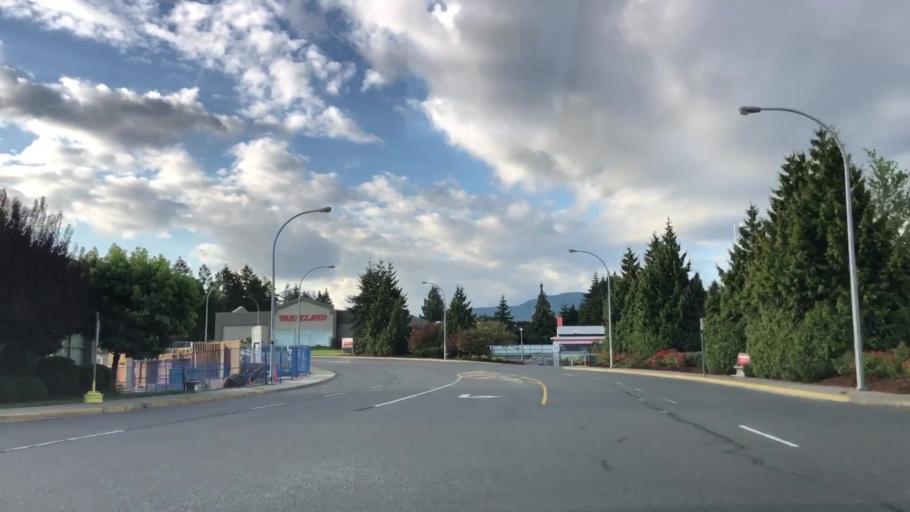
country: CA
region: British Columbia
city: Nanaimo
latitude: 49.2334
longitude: -124.0484
